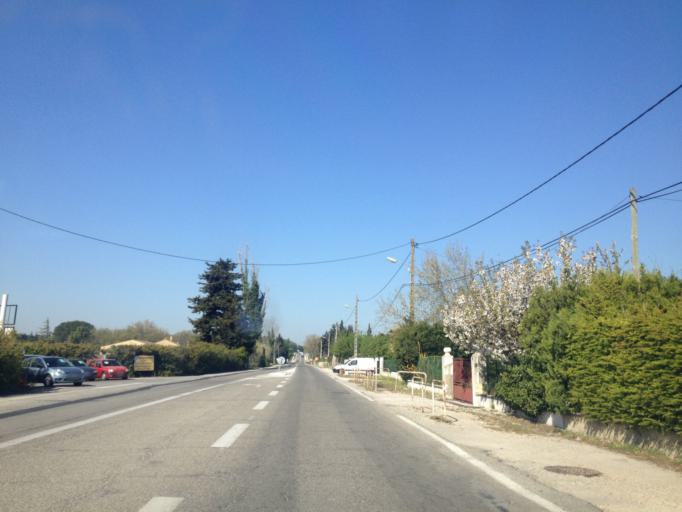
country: FR
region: Provence-Alpes-Cote d'Azur
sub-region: Departement du Vaucluse
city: Jonquieres
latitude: 44.1168
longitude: 4.8848
